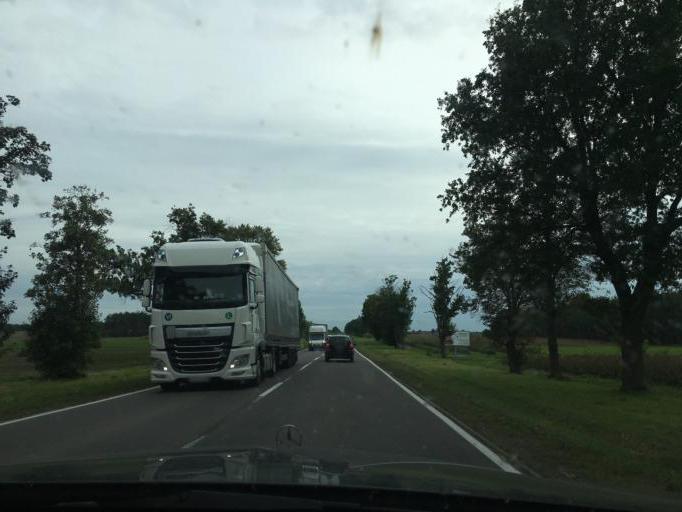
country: PL
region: Masovian Voivodeship
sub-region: Powiat ostrowski
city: Ostrow Mazowiecka
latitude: 52.8797
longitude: 21.8650
